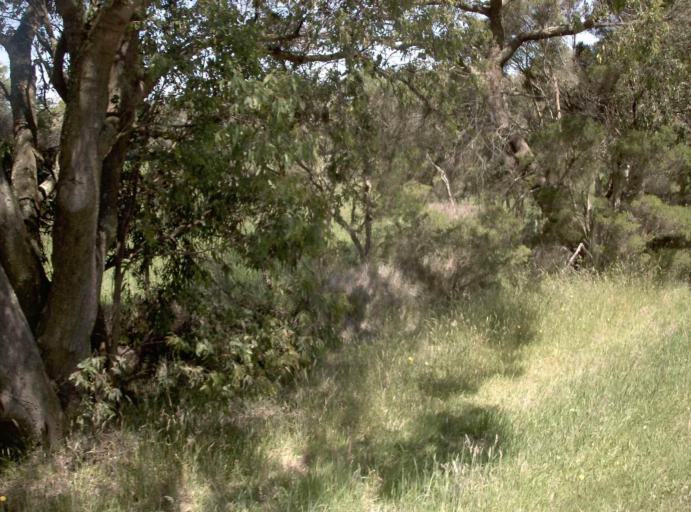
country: AU
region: Victoria
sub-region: Bass Coast
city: North Wonthaggi
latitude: -38.7705
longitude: 146.0646
